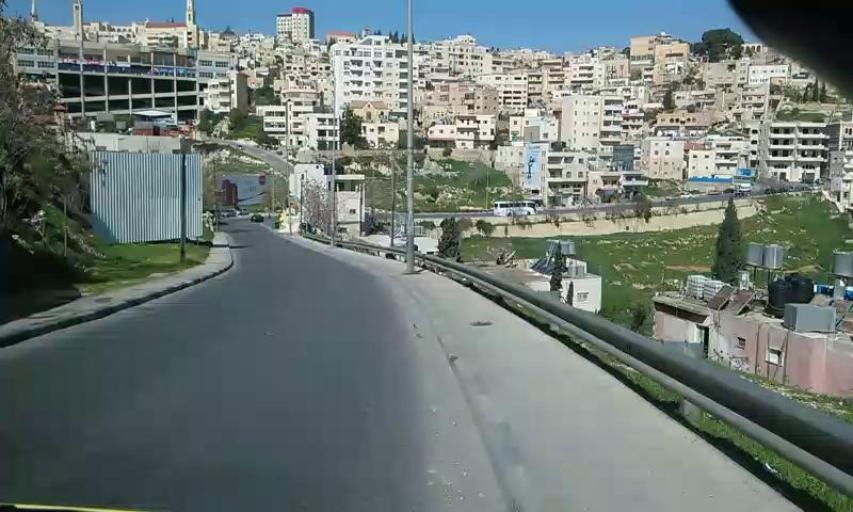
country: PS
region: West Bank
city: Bethlehem
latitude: 31.7058
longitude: 35.2091
